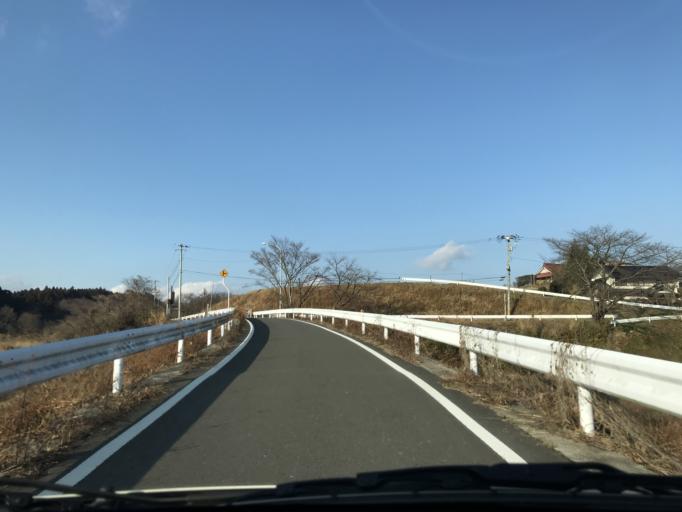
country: JP
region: Miyagi
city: Wakuya
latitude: 38.6899
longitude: 141.1066
